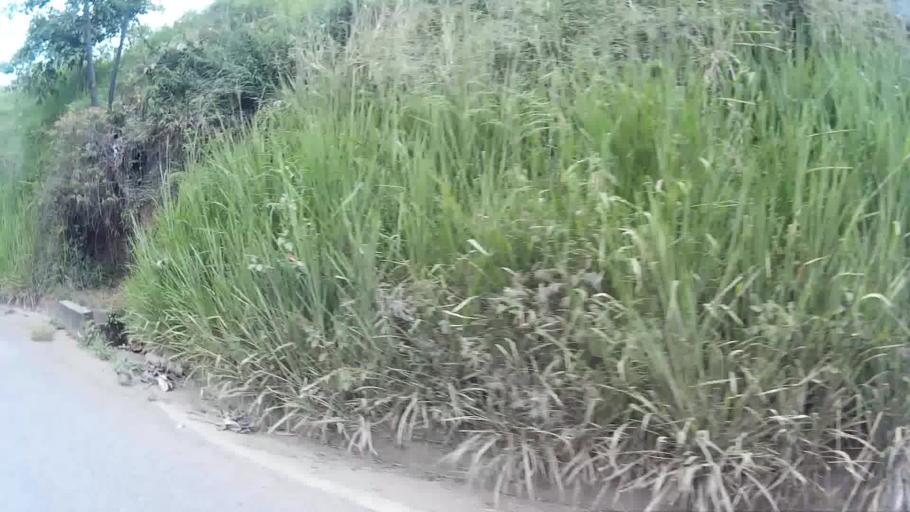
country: CO
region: Risaralda
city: Marsella
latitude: 4.8660
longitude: -75.7604
